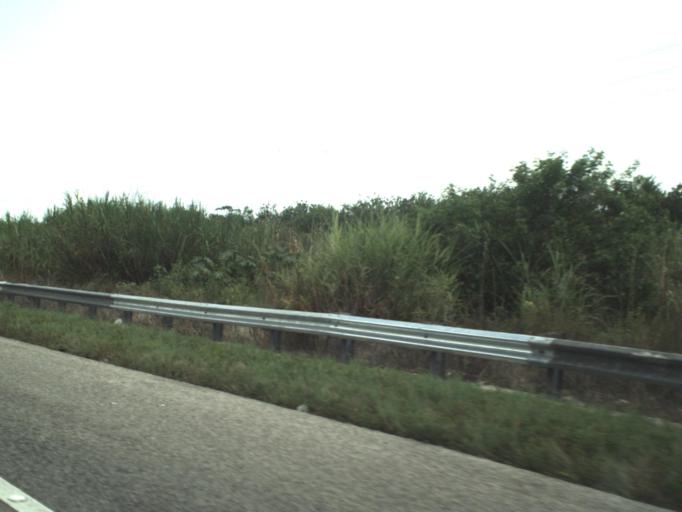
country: US
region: Florida
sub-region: Broward County
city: Weston
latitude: 26.3072
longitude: -80.5163
